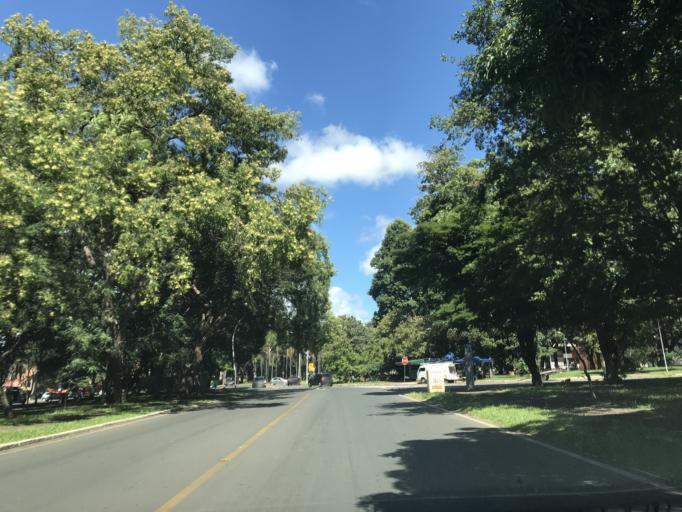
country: BR
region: Federal District
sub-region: Brasilia
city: Brasilia
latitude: -15.8231
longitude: -47.9033
